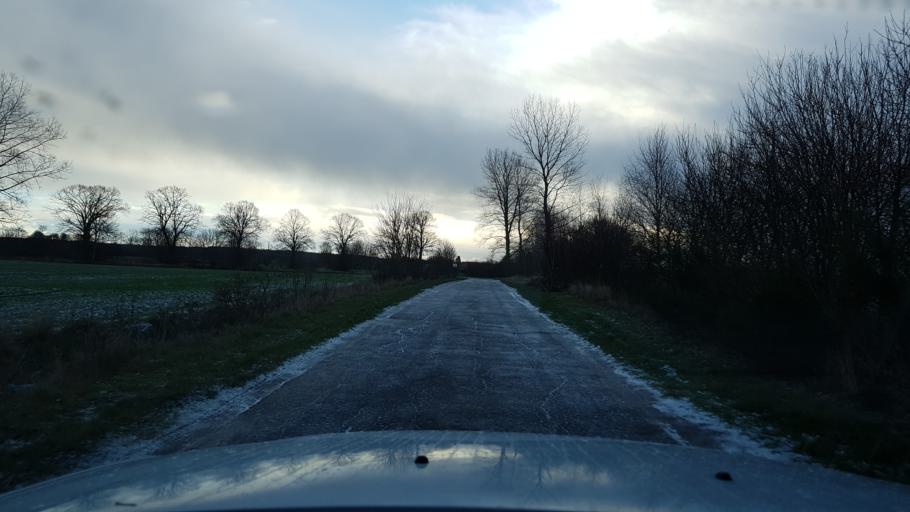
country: PL
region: West Pomeranian Voivodeship
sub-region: Powiat gryficki
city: Brojce
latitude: 54.0381
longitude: 15.3558
